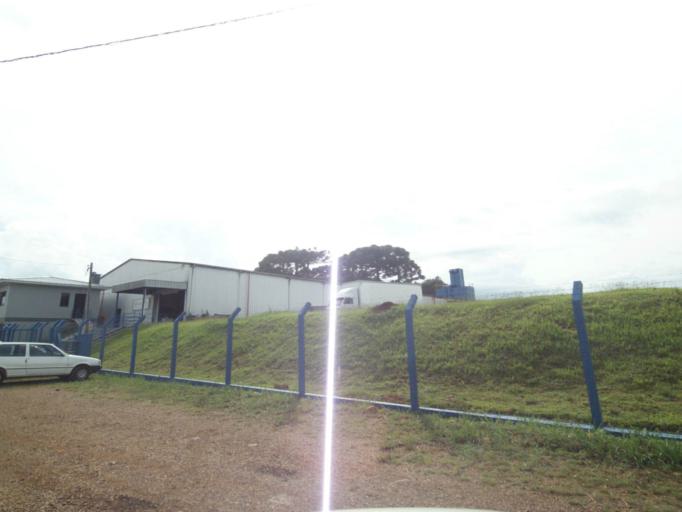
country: BR
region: Rio Grande do Sul
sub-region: Lagoa Vermelha
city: Lagoa Vermelha
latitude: -28.2327
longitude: -51.5165
